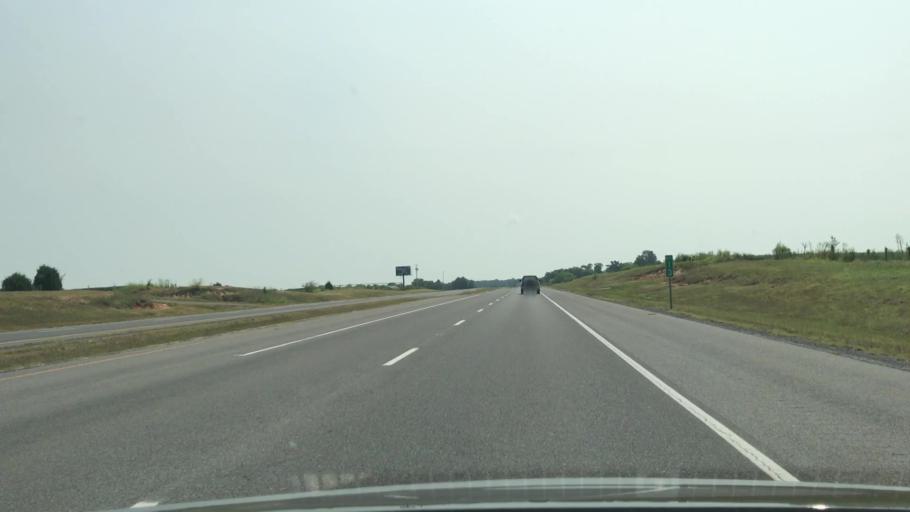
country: US
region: Kentucky
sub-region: Calloway County
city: Murray
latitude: 36.6499
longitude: -88.2591
